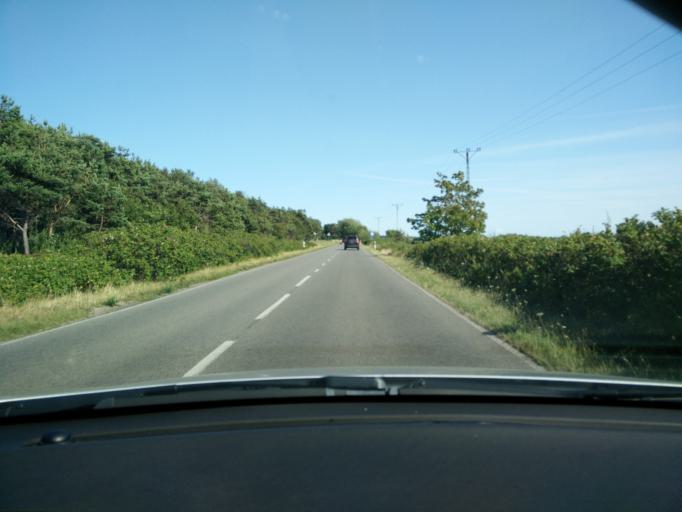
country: PL
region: Pomeranian Voivodeship
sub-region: Powiat pucki
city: Jastarnia
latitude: 54.7266
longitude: 18.6048
